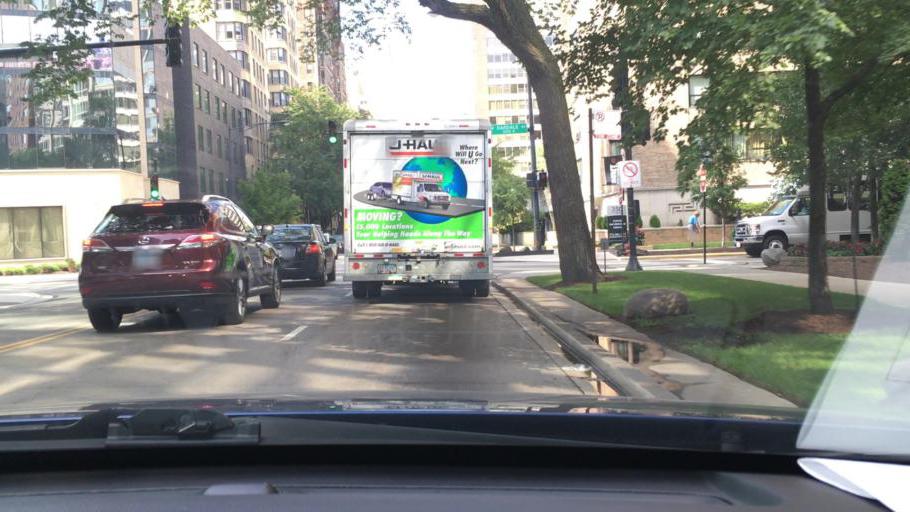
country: US
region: Illinois
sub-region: Cook County
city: Chicago
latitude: 41.9353
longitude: -87.6393
